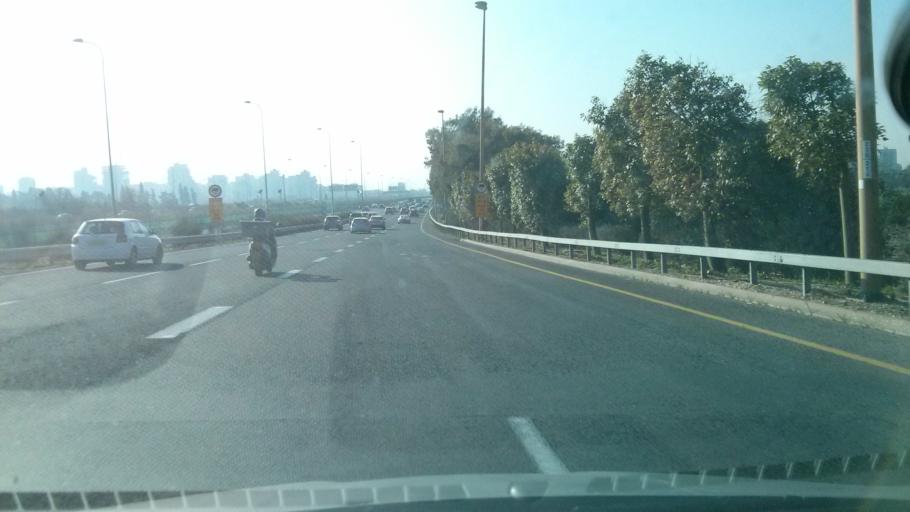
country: IL
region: Tel Aviv
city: Ramat HaSharon
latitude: 32.1371
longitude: 34.8094
